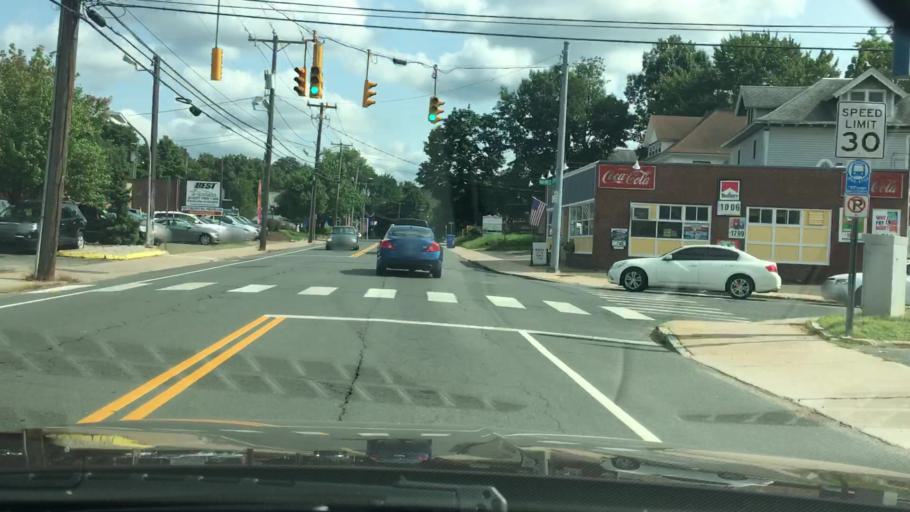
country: US
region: Connecticut
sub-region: Hartford County
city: Manchester
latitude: 41.7816
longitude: -72.5224
